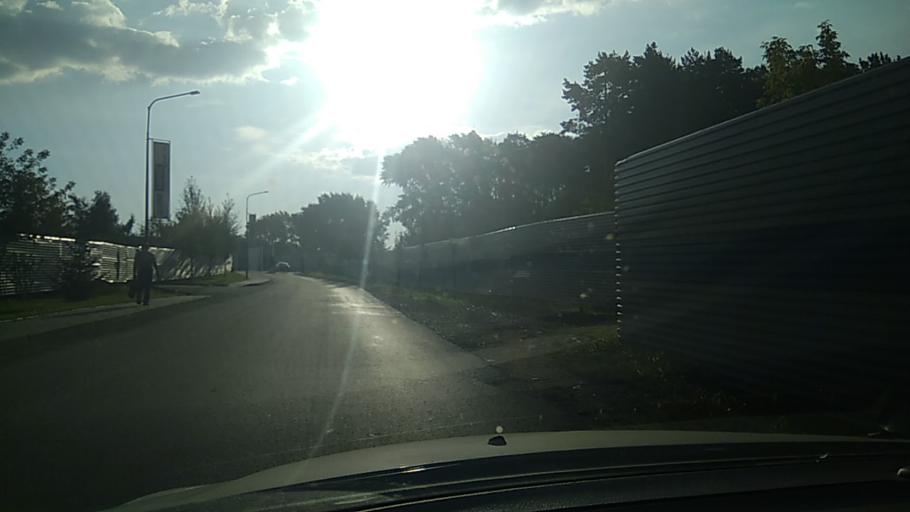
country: RU
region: Sverdlovsk
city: Yekaterinburg
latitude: 56.8178
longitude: 60.6478
